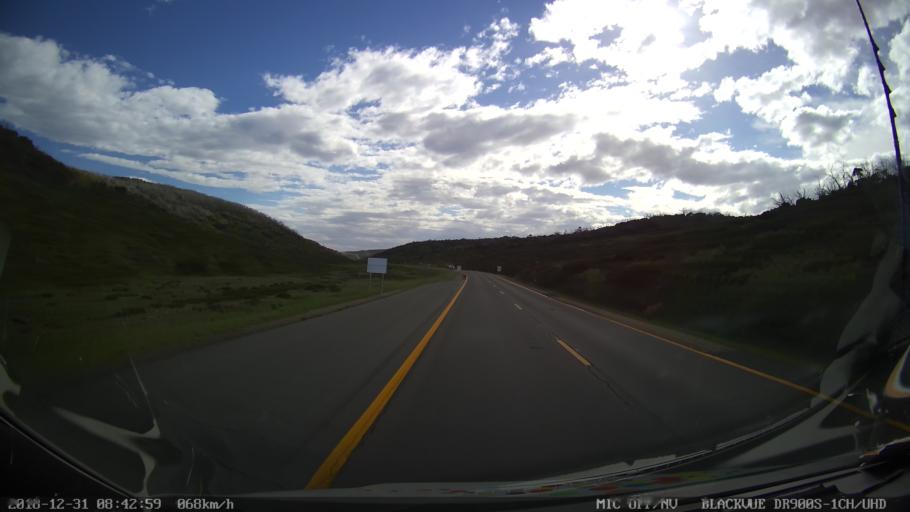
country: AU
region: New South Wales
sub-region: Snowy River
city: Jindabyne
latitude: -36.3916
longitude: 148.4394
